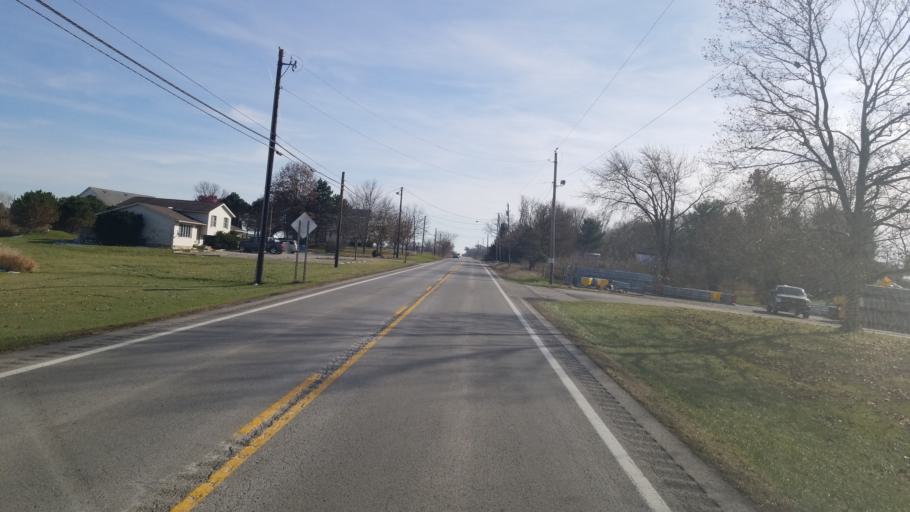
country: US
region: Ohio
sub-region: Huron County
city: Norwalk
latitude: 41.2087
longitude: -82.5875
